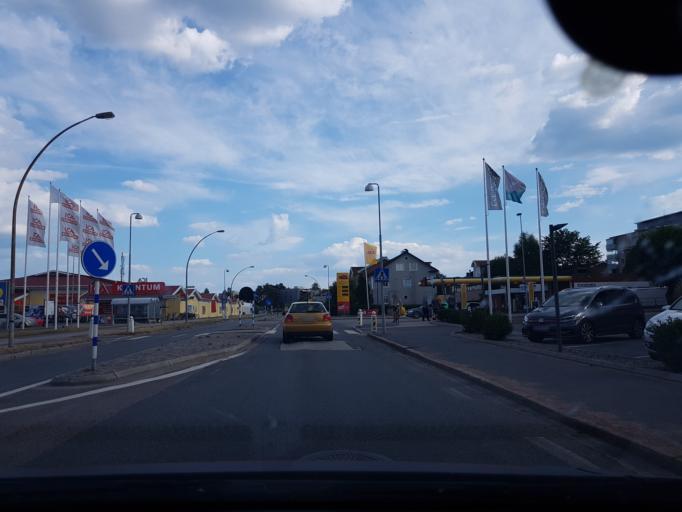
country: SE
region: Joenkoeping
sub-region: Gislaveds Kommun
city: Gislaved
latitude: 57.3040
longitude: 13.5426
